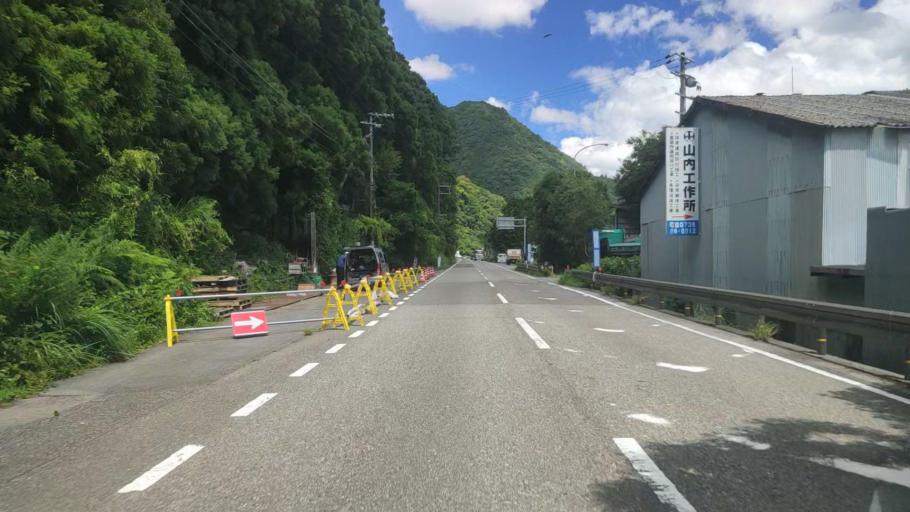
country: JP
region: Wakayama
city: Shingu
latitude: 33.7545
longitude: 135.9256
